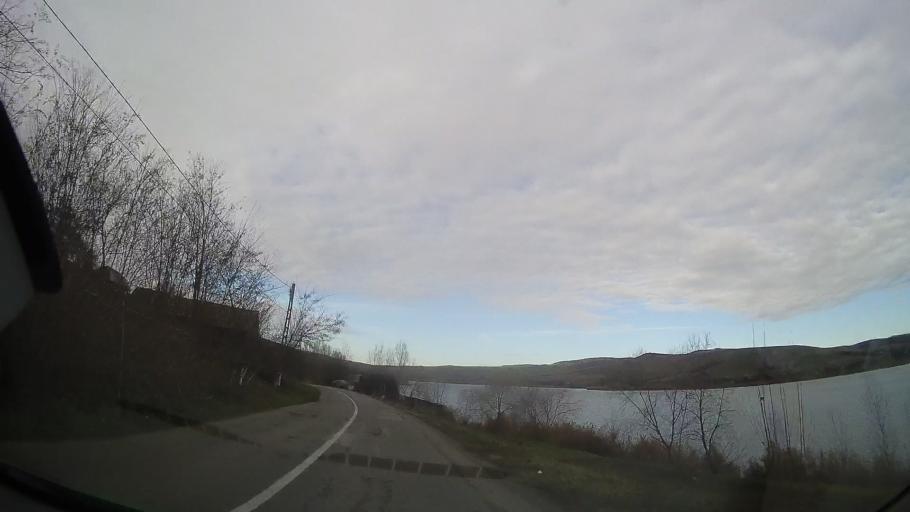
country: RO
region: Cluj
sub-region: Comuna Geaca
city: Geaca
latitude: 46.8390
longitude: 24.1294
